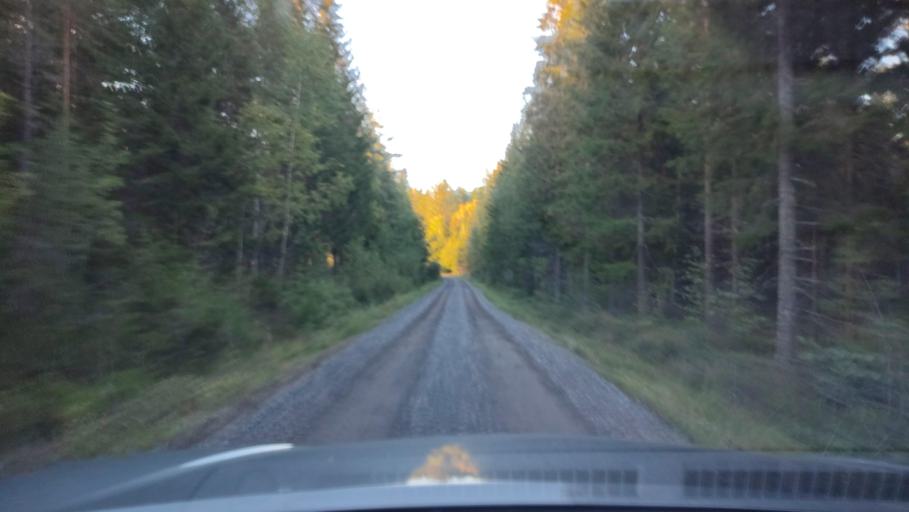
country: FI
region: Southern Ostrobothnia
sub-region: Suupohja
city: Karijoki
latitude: 62.2110
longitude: 21.5721
